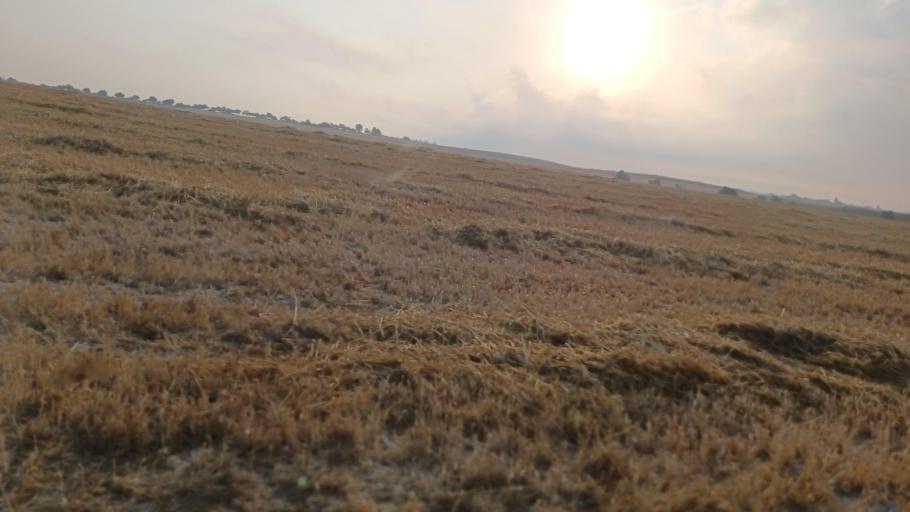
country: CY
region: Larnaka
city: Tersefanou
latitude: 34.8340
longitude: 33.5204
